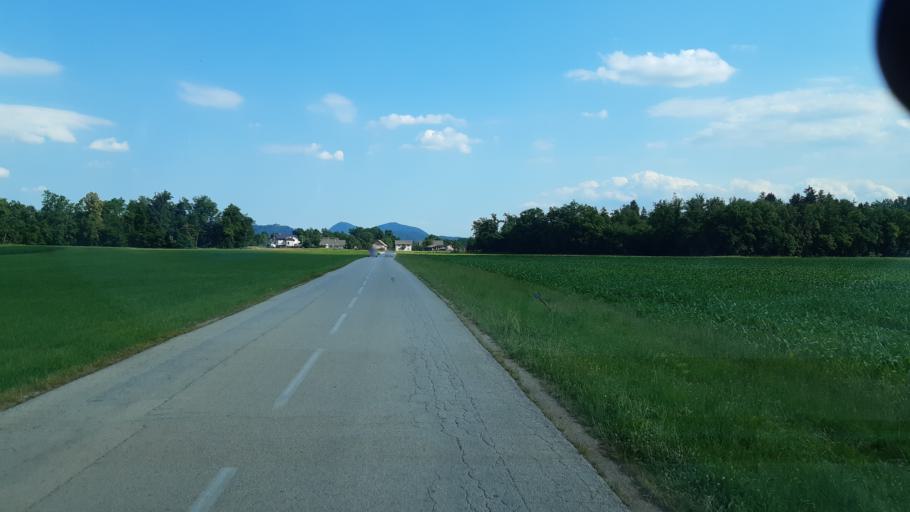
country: SI
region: Sencur
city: Hrastje
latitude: 46.2076
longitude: 14.4003
